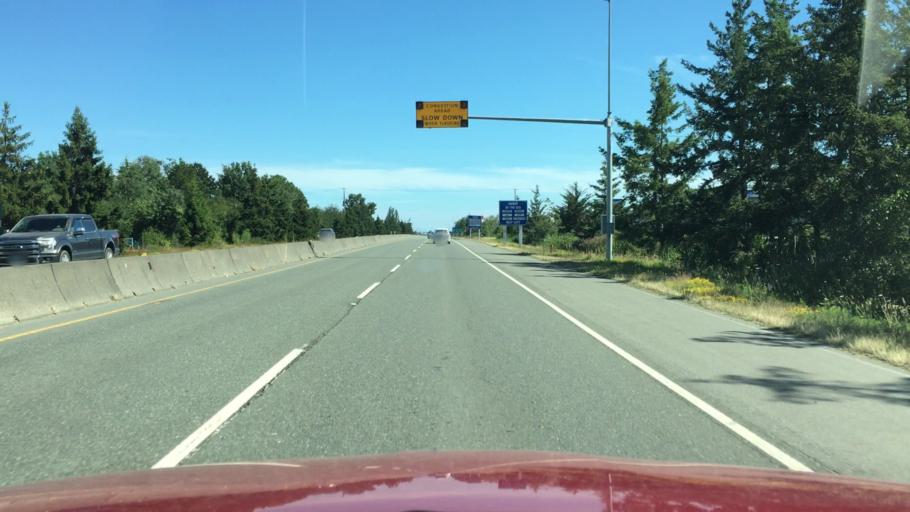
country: CA
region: British Columbia
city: North Saanich
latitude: 48.6575
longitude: -123.4134
